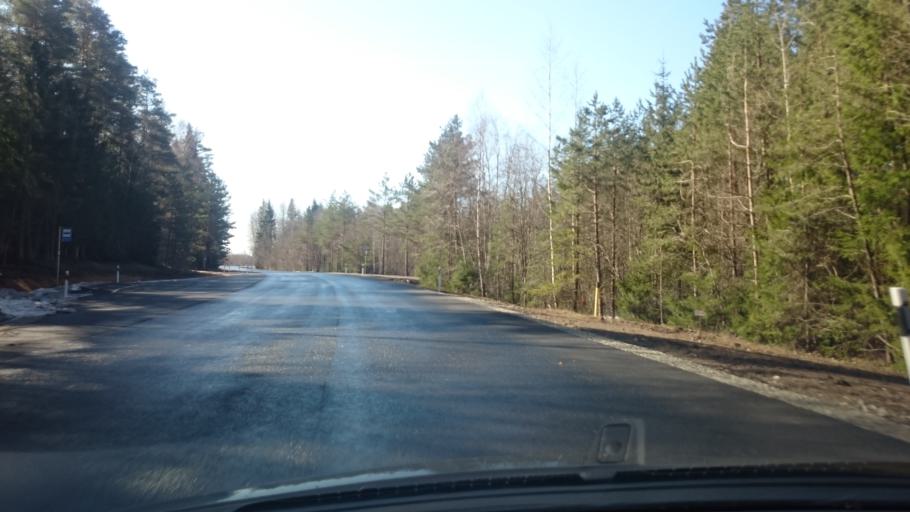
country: EE
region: Raplamaa
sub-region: Jaervakandi vald
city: Jarvakandi
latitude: 58.6958
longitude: 24.7833
